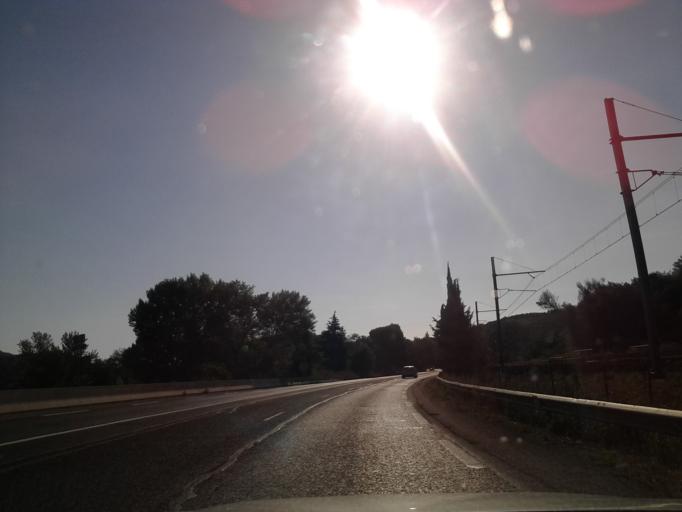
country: FR
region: Languedoc-Roussillon
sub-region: Departement des Pyrenees-Orientales
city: Vinca
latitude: 42.6510
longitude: 2.5357
